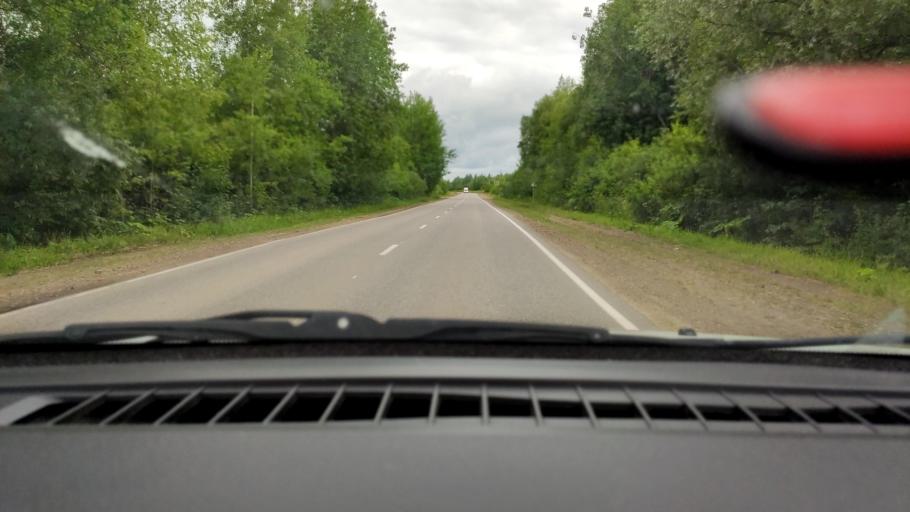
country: RU
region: Perm
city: Chaykovskaya
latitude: 58.0860
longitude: 55.6136
